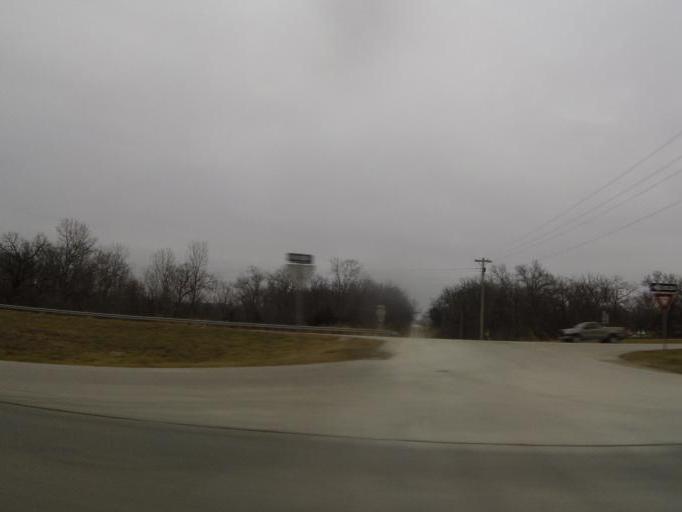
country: US
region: Missouri
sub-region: Ralls County
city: New London
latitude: 39.6421
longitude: -91.4197
